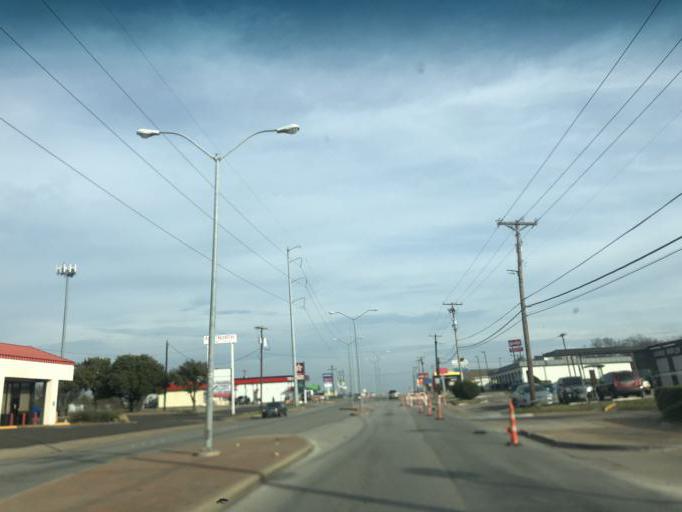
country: US
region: Texas
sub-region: Dallas County
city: Duncanville
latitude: 32.6619
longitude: -96.9003
